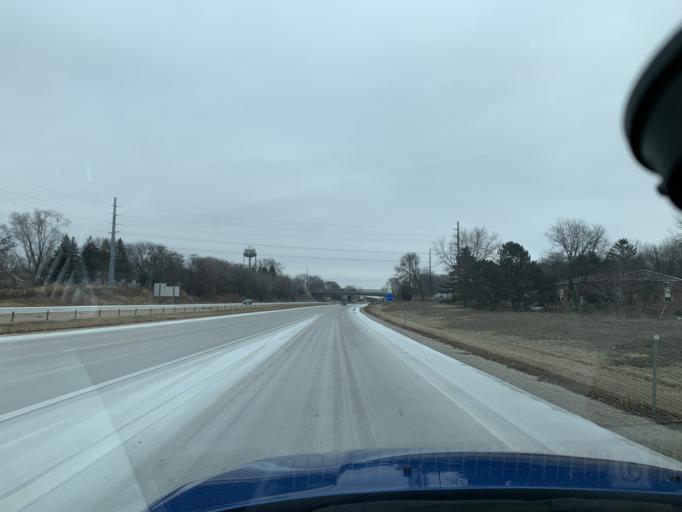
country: US
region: Wisconsin
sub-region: Dane County
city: Sun Prairie
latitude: 43.1899
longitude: -89.2294
